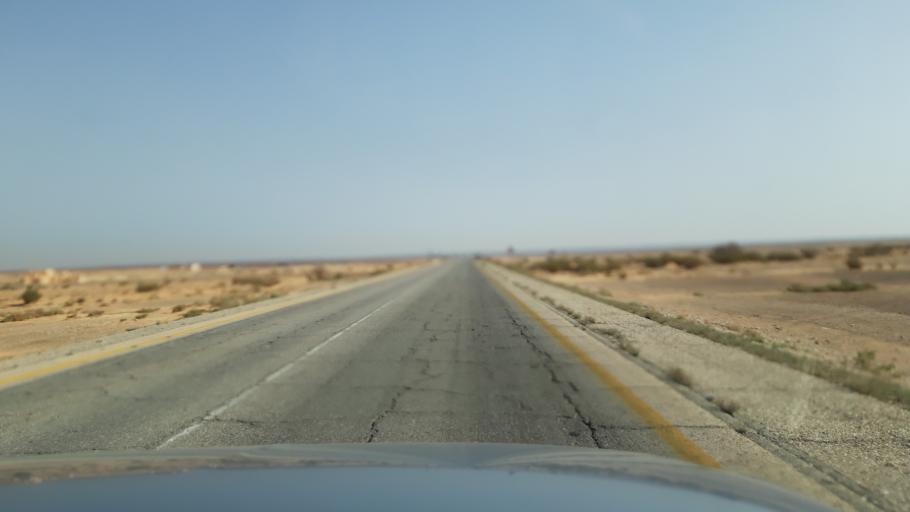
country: JO
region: Amman
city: Al Azraq ash Shamali
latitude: 31.7982
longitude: 36.5875
